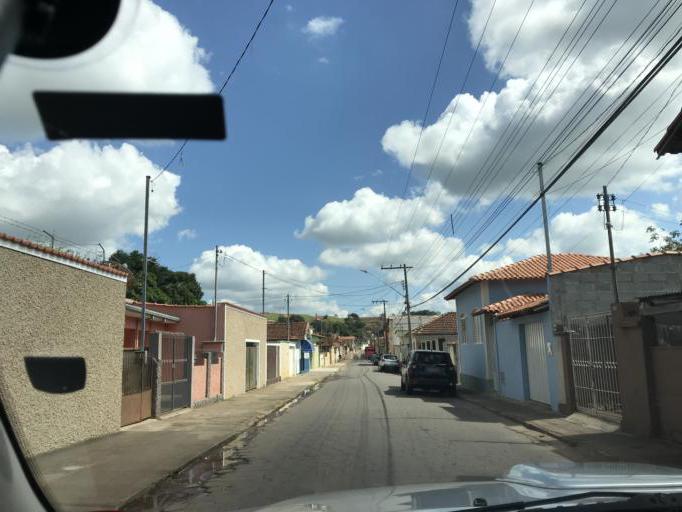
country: BR
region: Minas Gerais
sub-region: Campanha
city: Campanha
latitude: -21.8325
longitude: -45.4059
